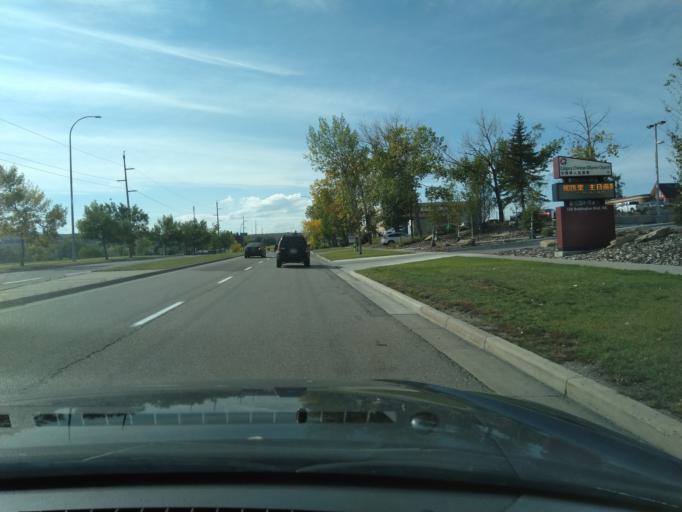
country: CA
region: Alberta
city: Calgary
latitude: 51.1253
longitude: -114.0677
